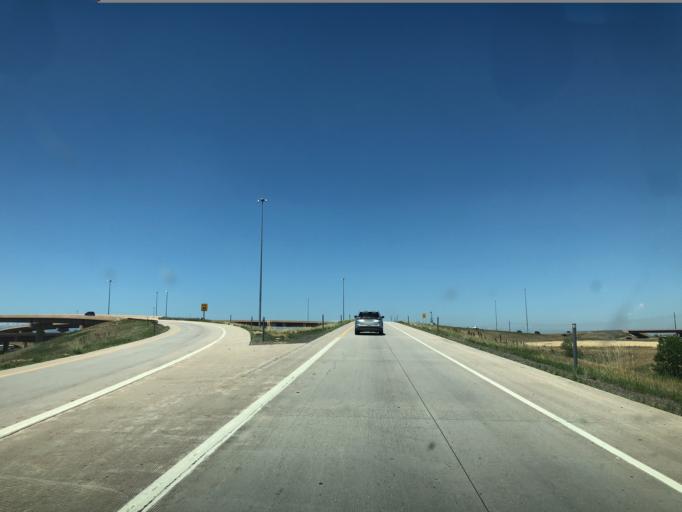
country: US
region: Colorado
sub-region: Boulder County
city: Erie
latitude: 39.9816
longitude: -104.9838
